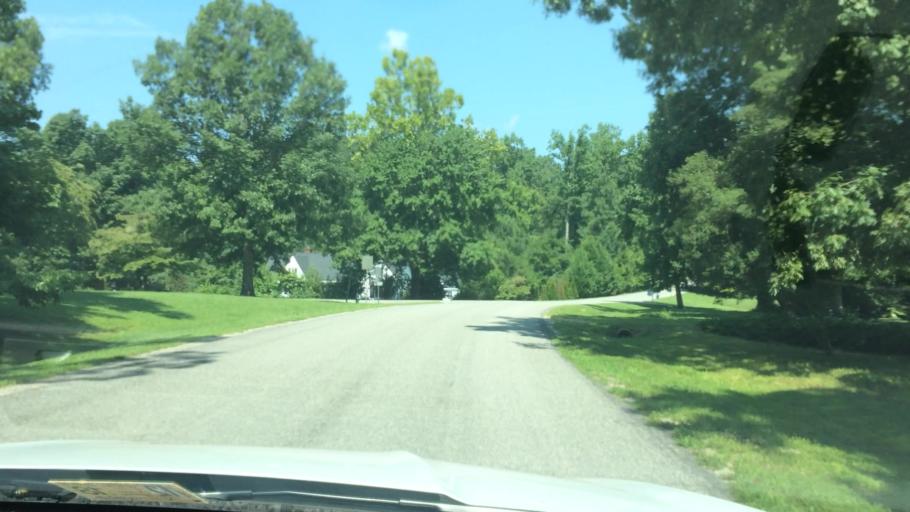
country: US
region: Virginia
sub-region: Henrico County
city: Sandston
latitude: 37.5035
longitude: -77.1711
